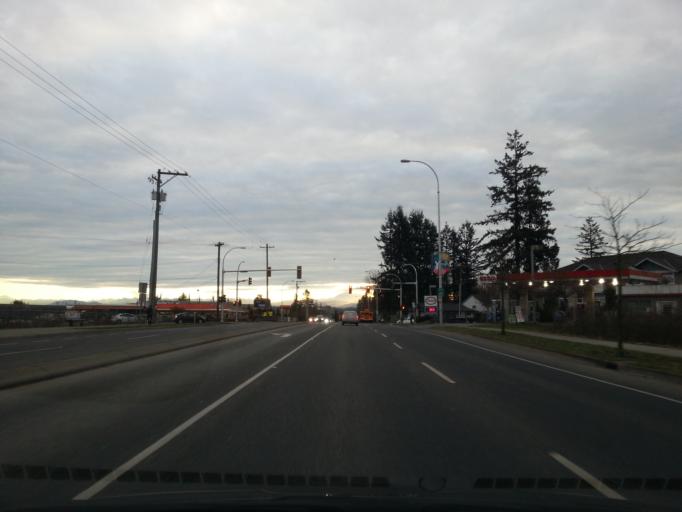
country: CA
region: British Columbia
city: Surrey
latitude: 49.1534
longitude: -122.7690
